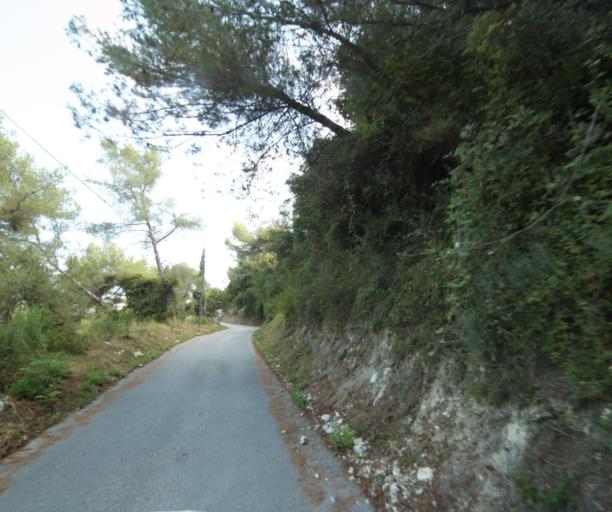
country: FR
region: Provence-Alpes-Cote d'Azur
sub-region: Departement des Alpes-Maritimes
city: Drap
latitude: 43.7610
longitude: 7.3492
